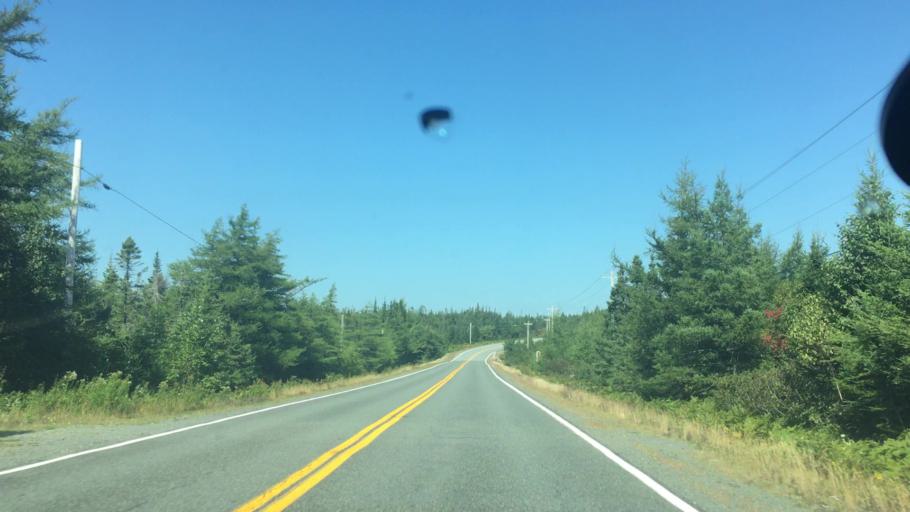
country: CA
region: Nova Scotia
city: Antigonish
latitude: 45.0060
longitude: -62.1042
